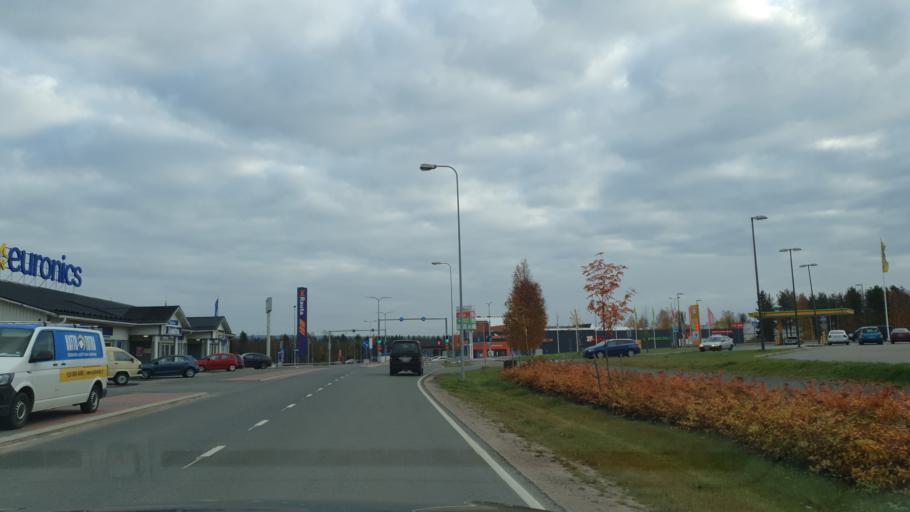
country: FI
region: Lapland
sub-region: Rovaniemi
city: Rovaniemi
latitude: 66.4933
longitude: 25.6885
